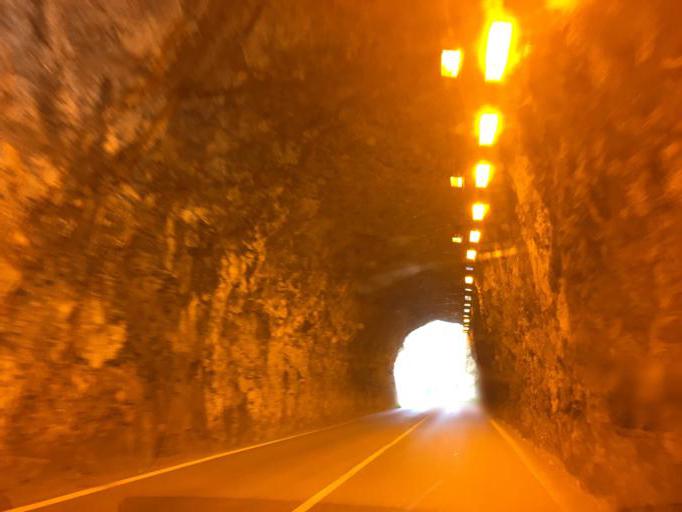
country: FR
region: Provence-Alpes-Cote d'Azur
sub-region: Departement des Alpes-Maritimes
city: Saint-Martin-Vesubie
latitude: 44.0545
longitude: 7.1221
